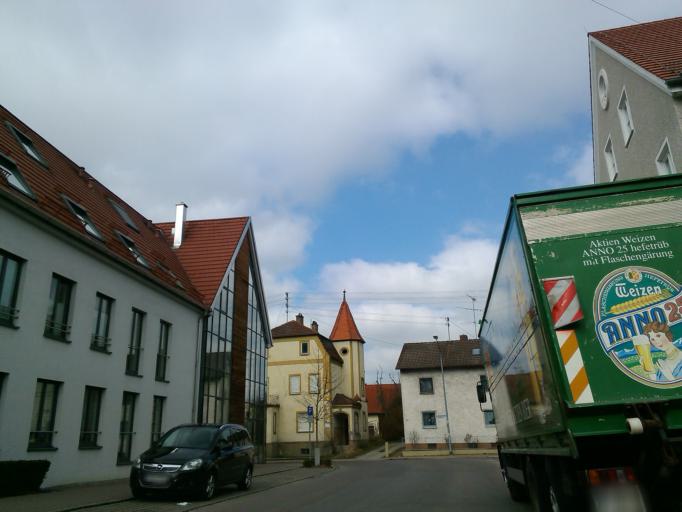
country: DE
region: Bavaria
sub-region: Swabia
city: Krumbach
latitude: 48.2451
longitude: 10.3689
